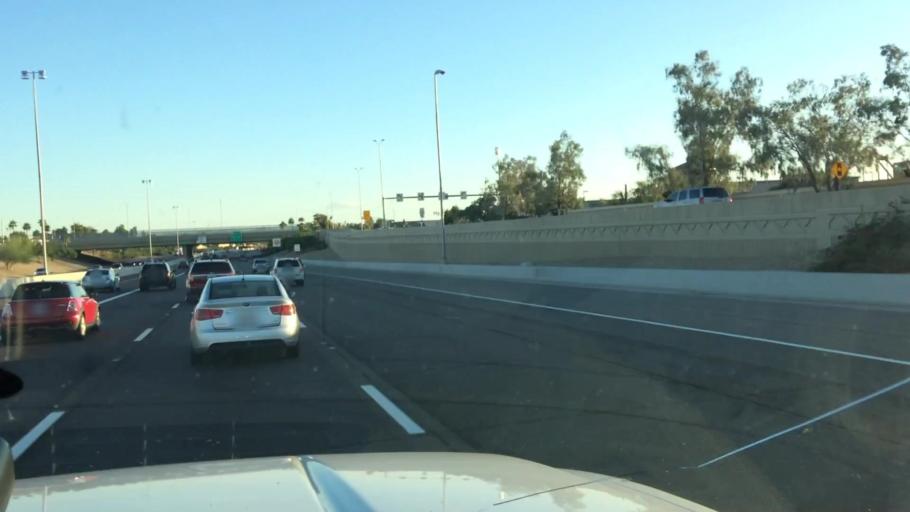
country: US
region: Arizona
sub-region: Maricopa County
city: Sun City
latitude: 33.6553
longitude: -112.2333
